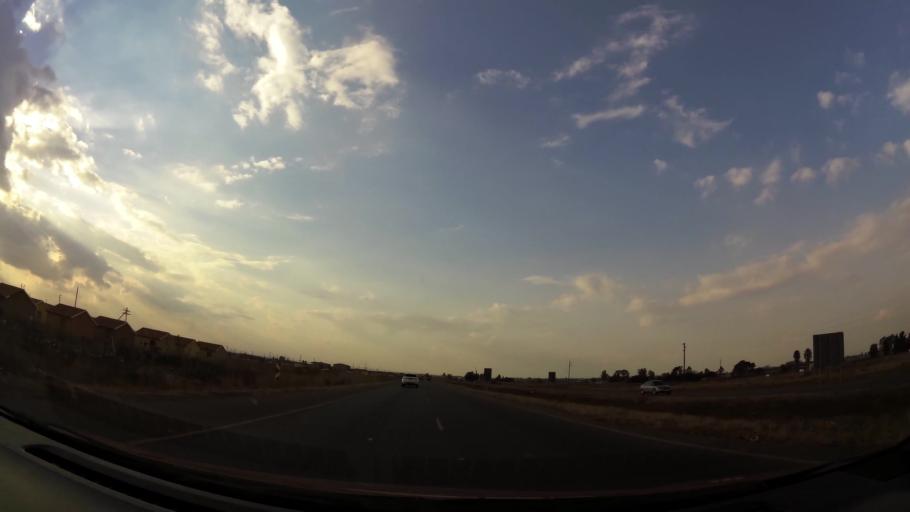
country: ZA
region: Gauteng
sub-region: Sedibeng District Municipality
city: Vanderbijlpark
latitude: -26.6168
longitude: 27.8133
